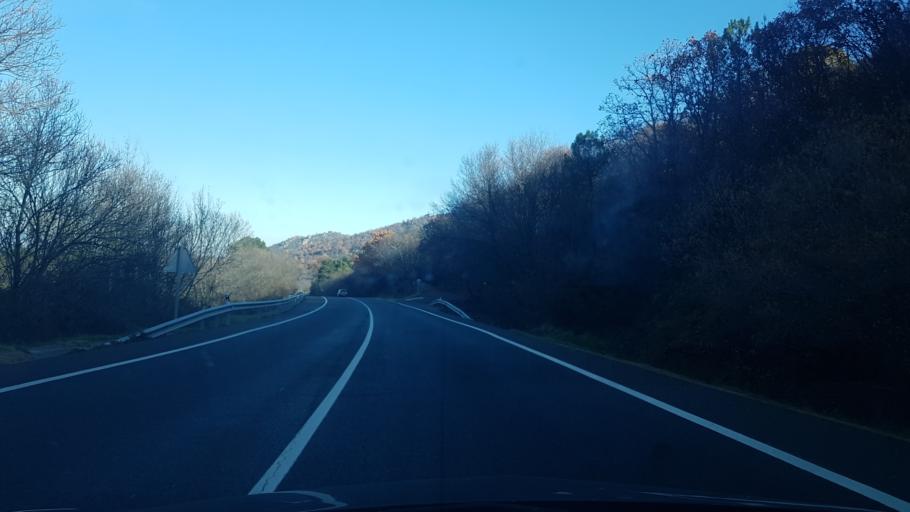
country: ES
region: Castille and Leon
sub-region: Provincia de Avila
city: Navahondilla
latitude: 40.3108
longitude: -4.5130
